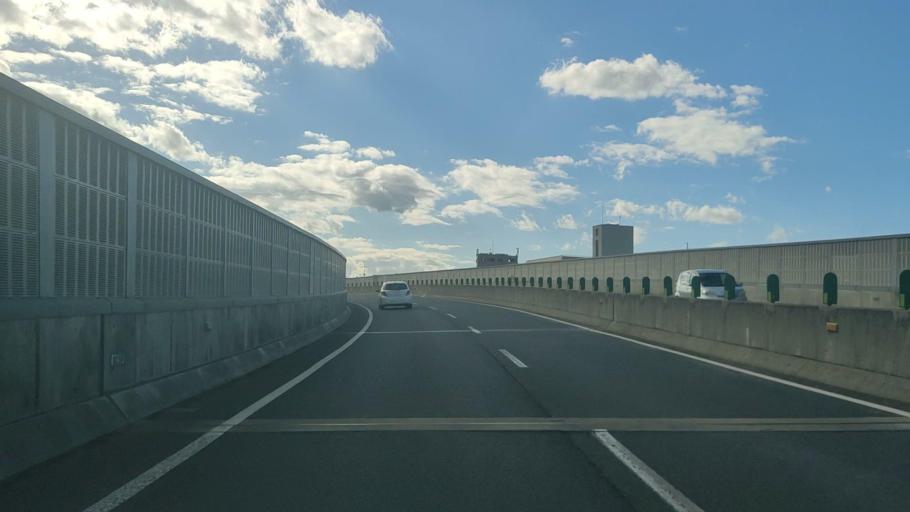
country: JP
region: Yamaguchi
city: Shimonoseki
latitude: 33.8842
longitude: 130.9072
